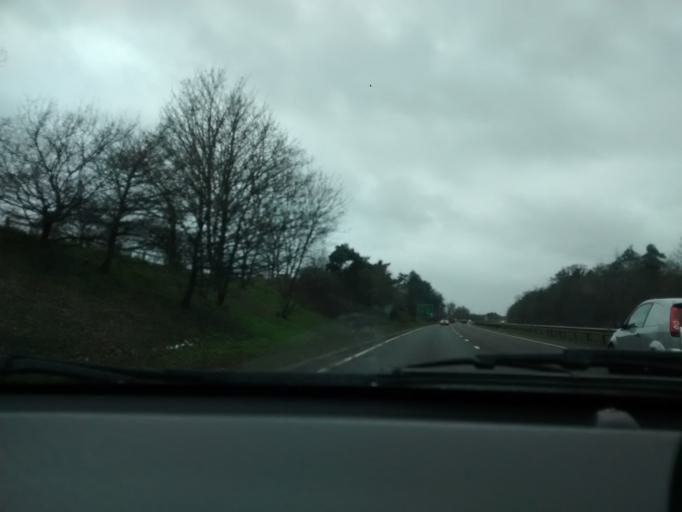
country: GB
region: England
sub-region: Suffolk
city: Needham Market
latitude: 52.1335
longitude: 1.0909
